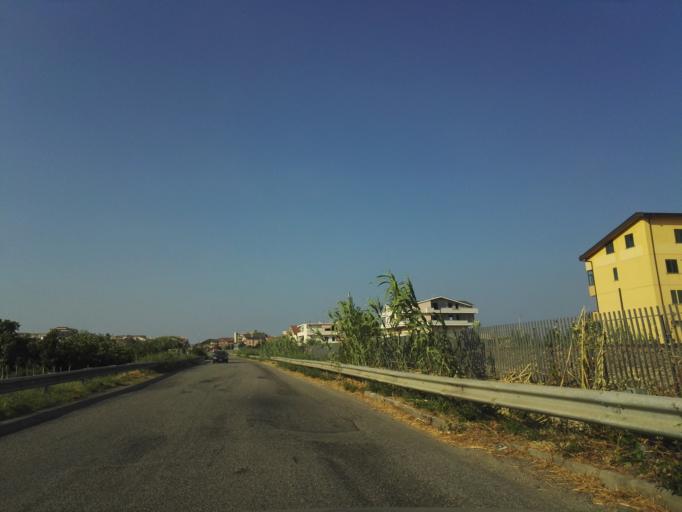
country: IT
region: Calabria
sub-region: Provincia di Reggio Calabria
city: Monasterace Marina
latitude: 38.4289
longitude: 16.5702
